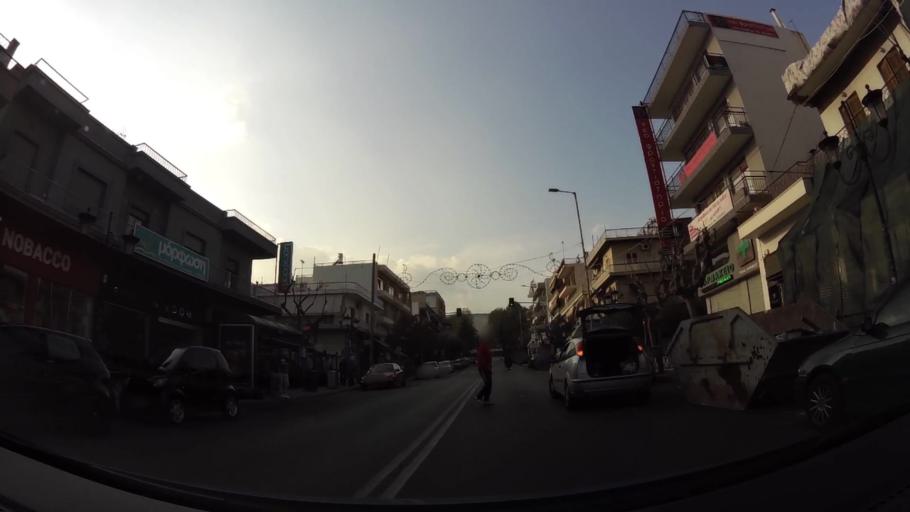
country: GR
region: Attica
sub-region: Nomarchia Athinas
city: Petroupolis
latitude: 38.0418
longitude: 23.6854
